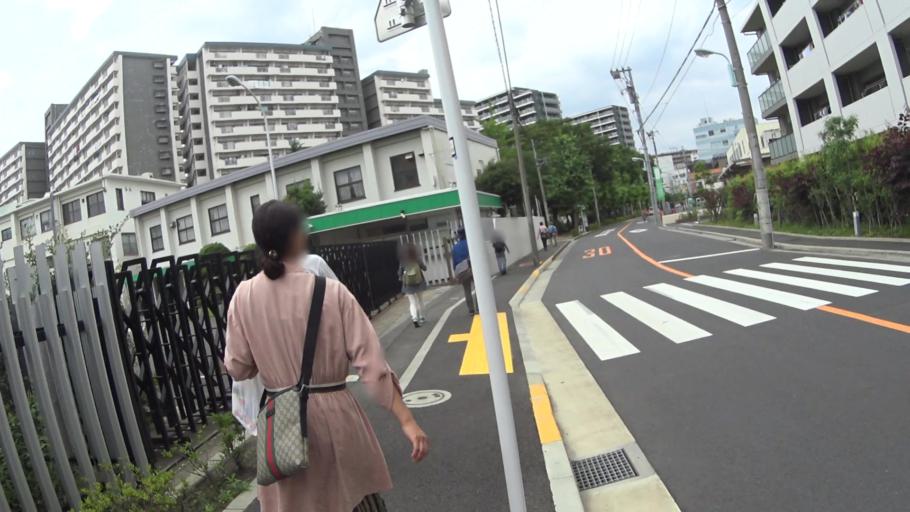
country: JP
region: Tokyo
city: Urayasu
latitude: 35.7140
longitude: 139.8366
